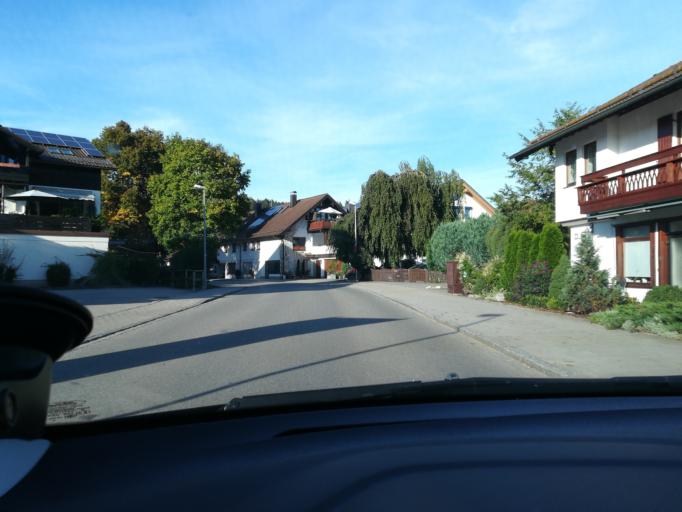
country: DE
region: Bavaria
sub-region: Upper Bavaria
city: Feldkirchen-Westerham
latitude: 47.9079
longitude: 11.8446
